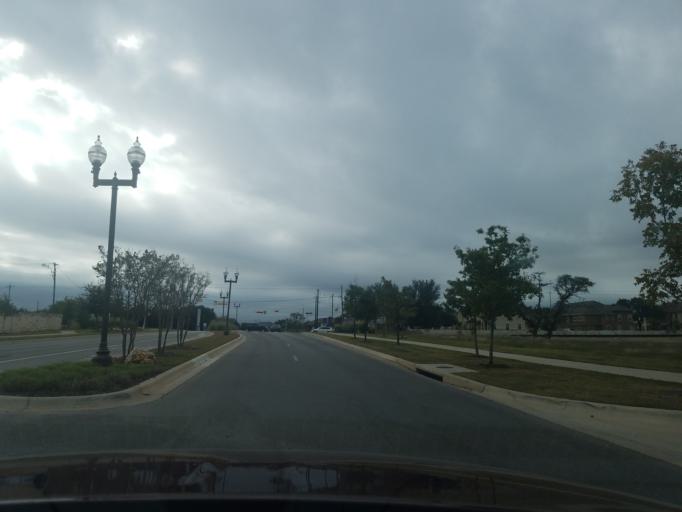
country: US
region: Texas
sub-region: Williamson County
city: Anderson Mill
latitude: 30.4829
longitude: -97.7900
